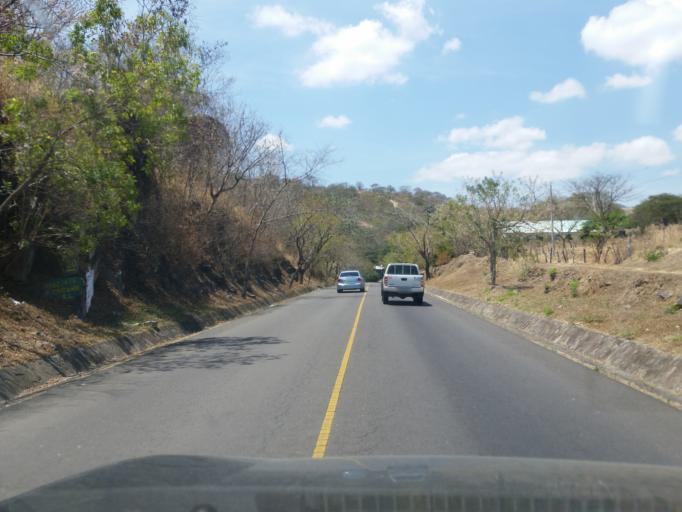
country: NI
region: Esteli
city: Esteli
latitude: 12.9969
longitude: -86.2913
